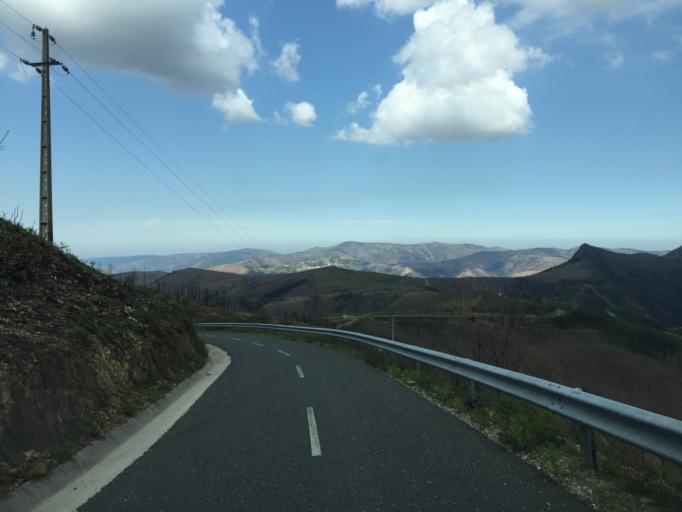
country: PT
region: Coimbra
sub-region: Pampilhosa da Serra
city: Pampilhosa da Serra
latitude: 40.1398
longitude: -7.9095
